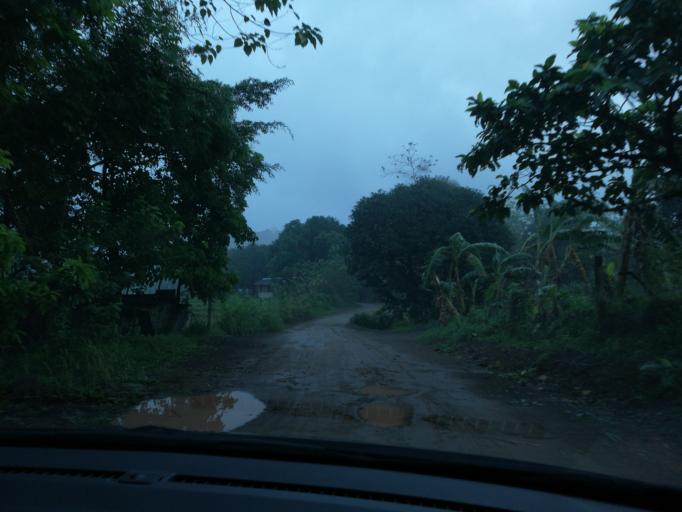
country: PH
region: Calabarzon
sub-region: Province of Rizal
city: Rodriguez
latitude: 14.7924
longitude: 121.1439
